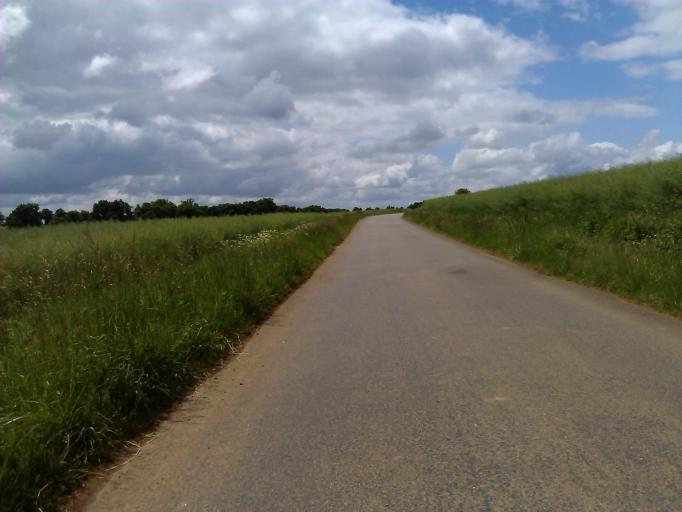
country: FR
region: Poitou-Charentes
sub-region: Departement de la Charente
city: Champagne-Mouton
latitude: 46.0677
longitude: 0.4875
